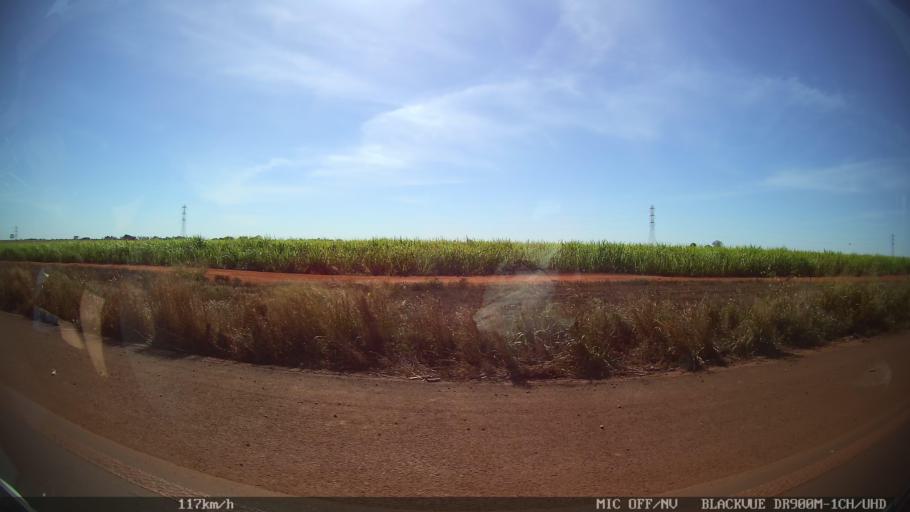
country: BR
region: Sao Paulo
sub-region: Guaira
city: Guaira
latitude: -20.4462
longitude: -48.4251
